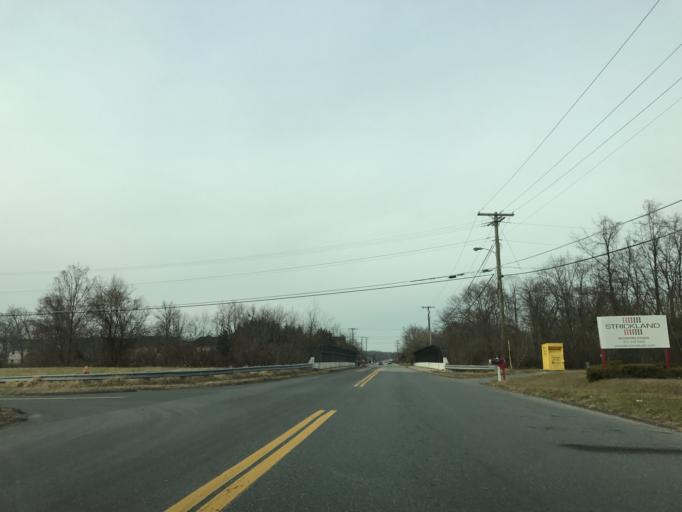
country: US
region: Maryland
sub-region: Baltimore County
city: White Marsh
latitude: 39.4000
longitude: -76.4065
